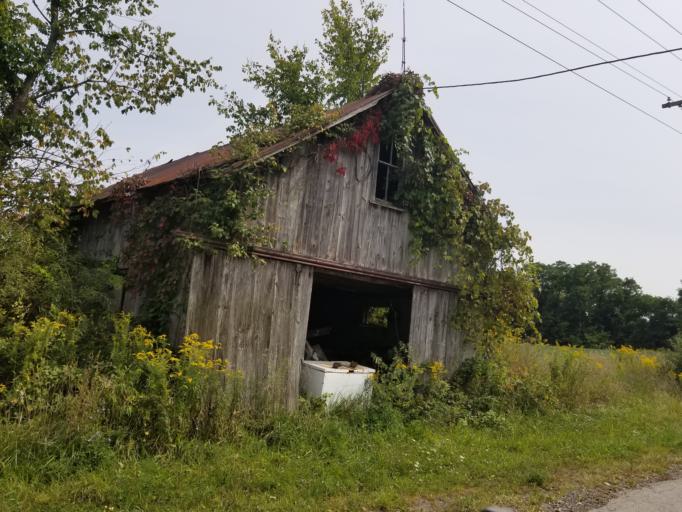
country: US
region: Ohio
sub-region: Knox County
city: Centerburg
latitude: 40.4149
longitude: -82.6510
